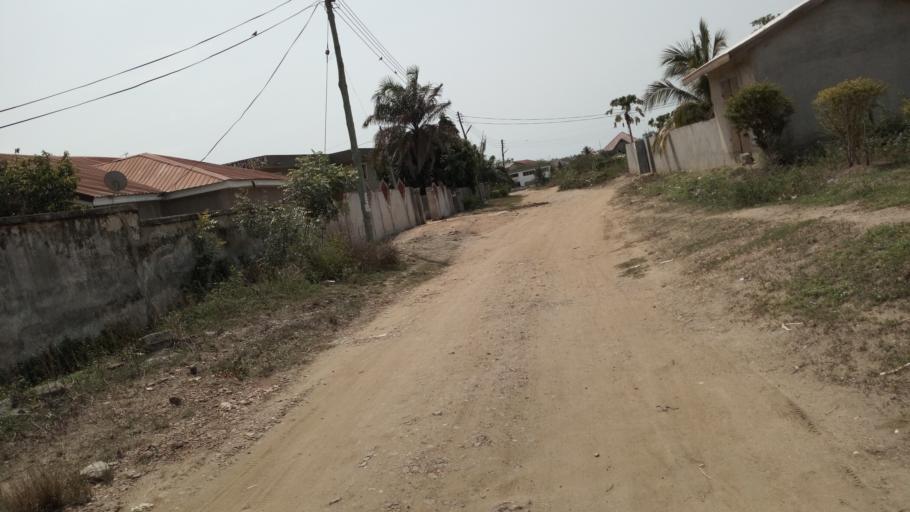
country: GH
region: Central
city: Winneba
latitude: 5.3673
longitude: -0.6439
